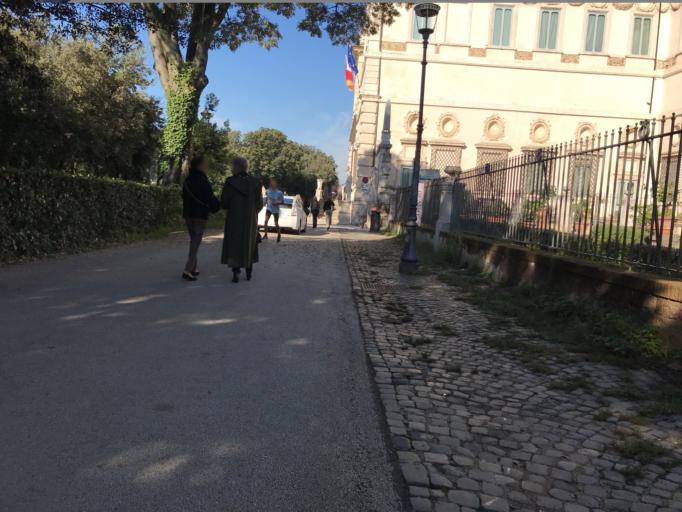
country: IT
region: Latium
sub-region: Citta metropolitana di Roma Capitale
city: Rome
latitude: 41.9137
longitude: 12.4927
